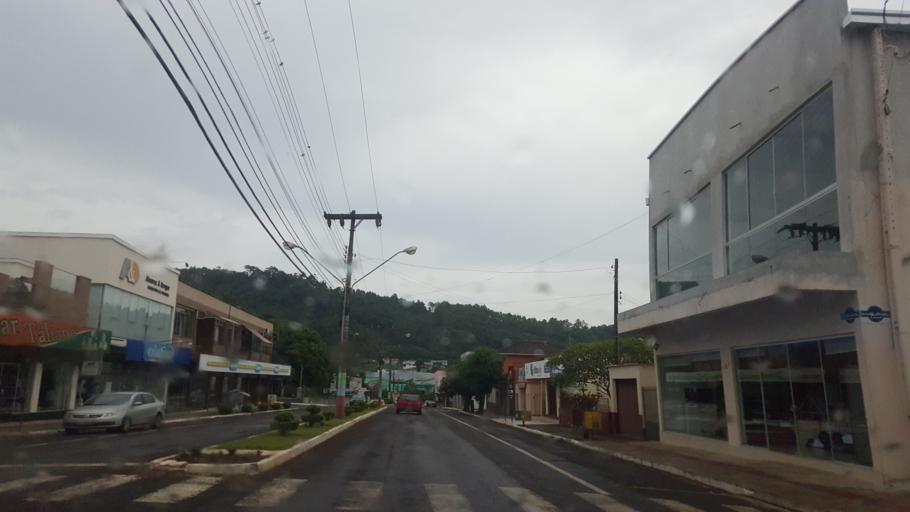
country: BR
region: Rio Grande do Sul
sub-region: Frederico Westphalen
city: Frederico Westphalen
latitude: -27.1034
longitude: -53.3991
